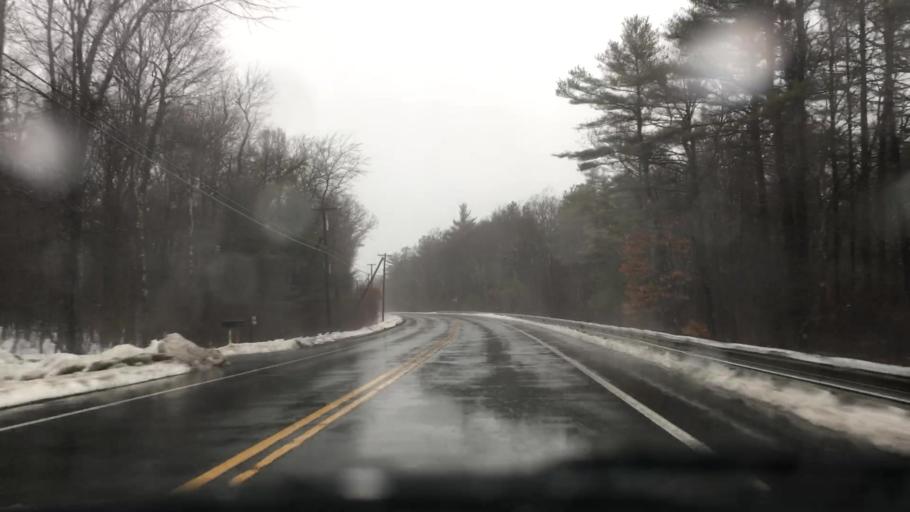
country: US
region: Massachusetts
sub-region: Hampshire County
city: Pelham
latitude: 42.3805
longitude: -72.4010
